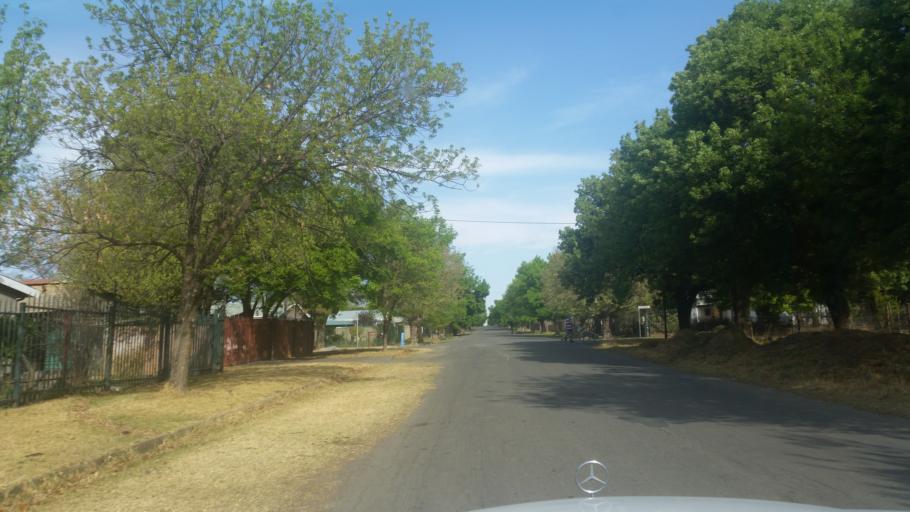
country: ZA
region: Orange Free State
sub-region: Thabo Mofutsanyana District Municipality
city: Harrismith
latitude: -28.2628
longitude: 29.1201
